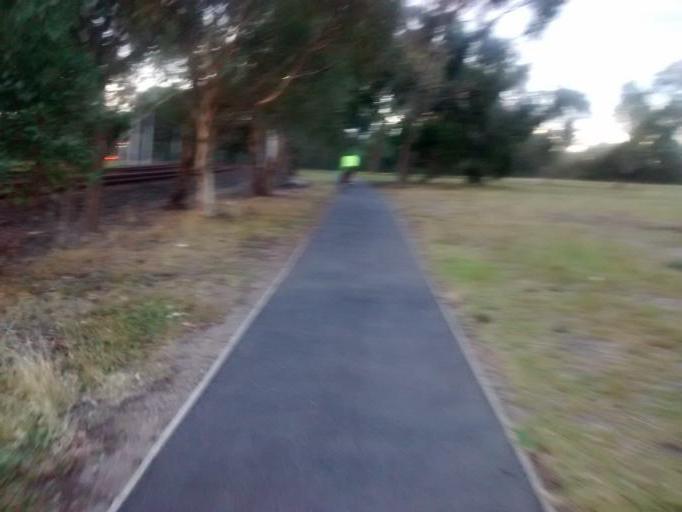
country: AU
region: Victoria
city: Parkville
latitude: -37.7910
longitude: 144.9497
